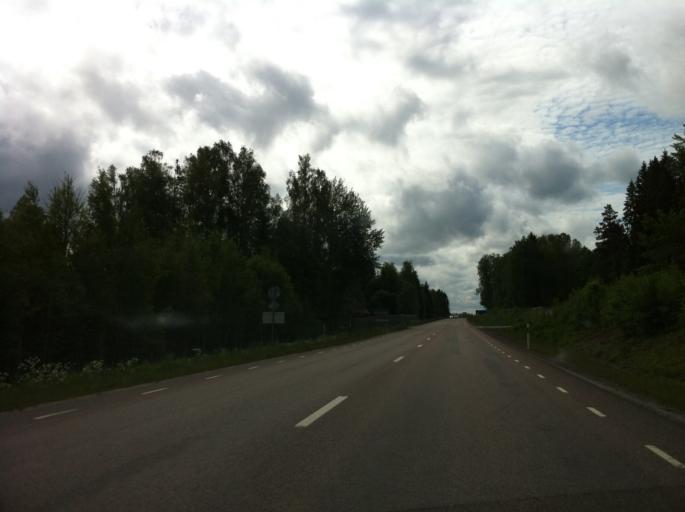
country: SE
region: Vaermland
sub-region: Sunne Kommun
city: Sunne
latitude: 59.7443
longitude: 13.1271
